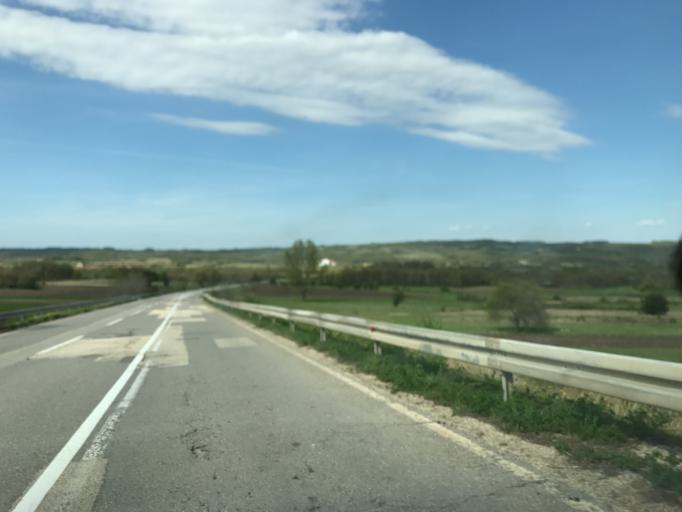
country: RS
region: Central Serbia
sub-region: Zajecarski Okrug
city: Zajecar
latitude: 44.0807
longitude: 22.3375
